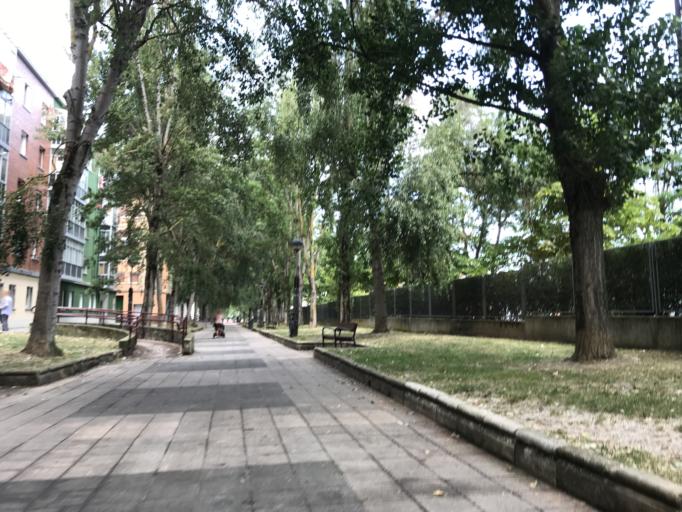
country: ES
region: Basque Country
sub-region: Provincia de Alava
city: Gasteiz / Vitoria
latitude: 42.8376
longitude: -2.6626
